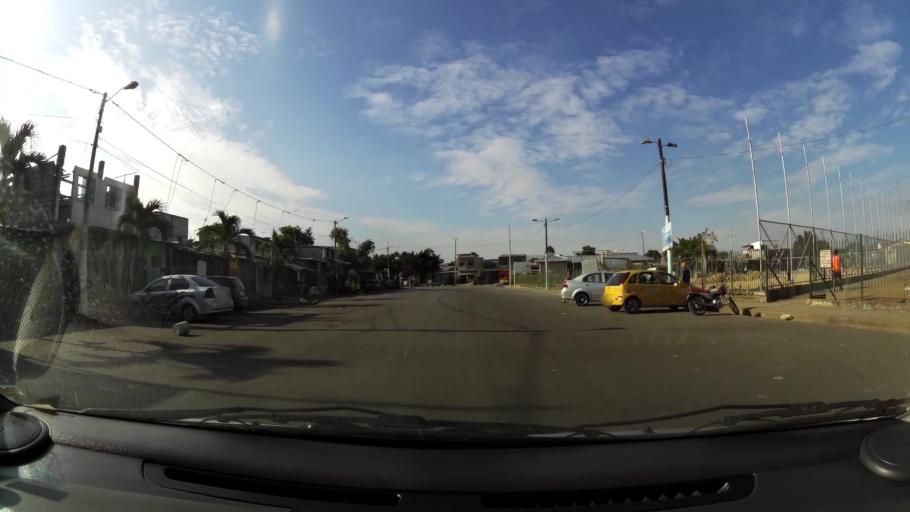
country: EC
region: Guayas
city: Guayaquil
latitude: -2.2232
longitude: -79.9175
